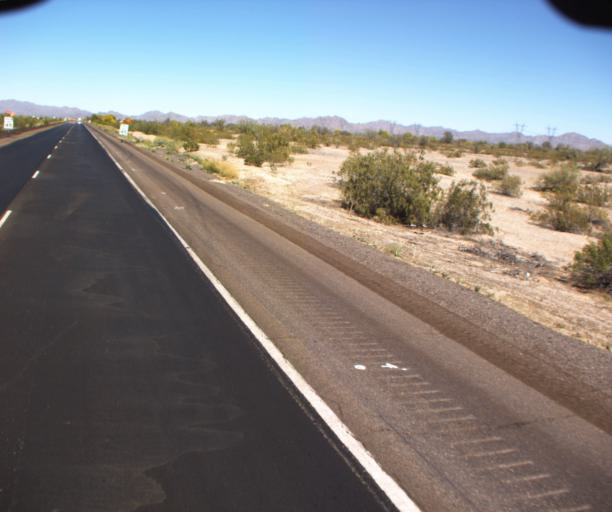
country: US
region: Arizona
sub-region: Maricopa County
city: Gila Bend
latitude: 32.9846
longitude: -112.6664
